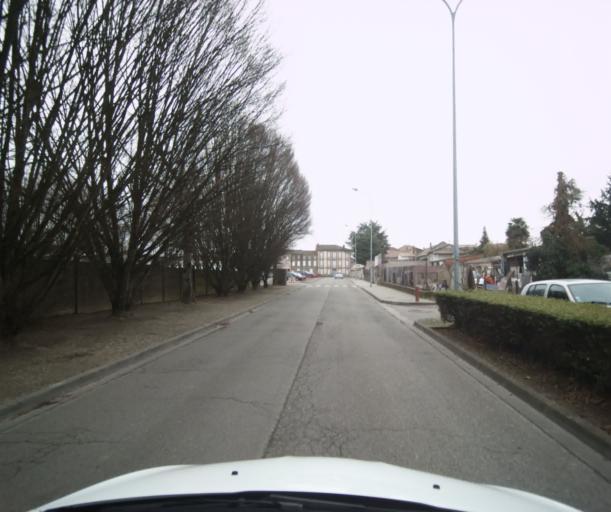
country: FR
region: Midi-Pyrenees
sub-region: Departement du Tarn-et-Garonne
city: Castelsarrasin
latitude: 44.0417
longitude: 1.1083
